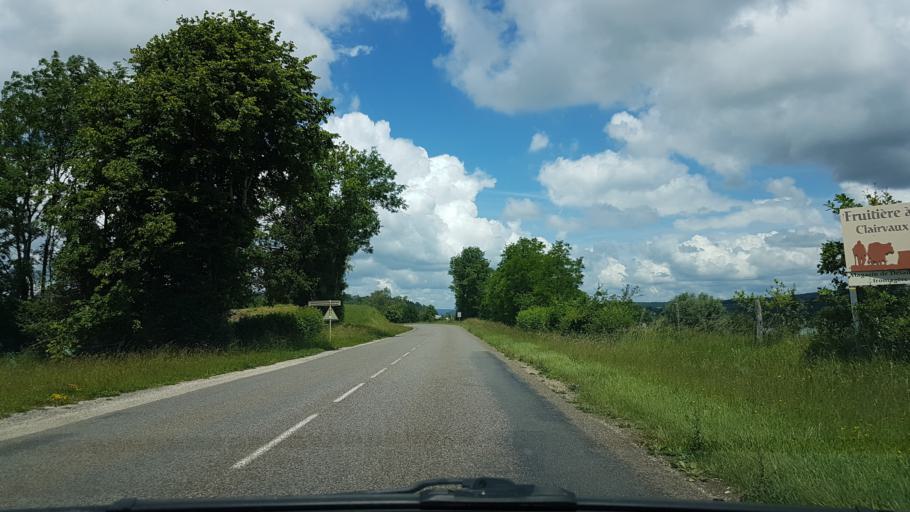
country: FR
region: Franche-Comte
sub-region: Departement du Jura
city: Clairvaux-les-Lacs
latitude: 46.5573
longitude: 5.7449
